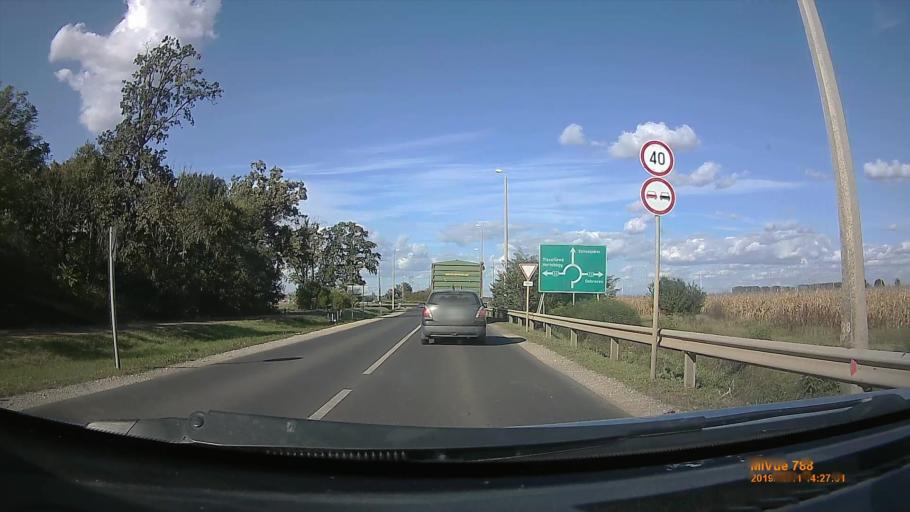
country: HU
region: Hajdu-Bihar
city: Balmazujvaros
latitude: 47.5544
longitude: 21.3575
